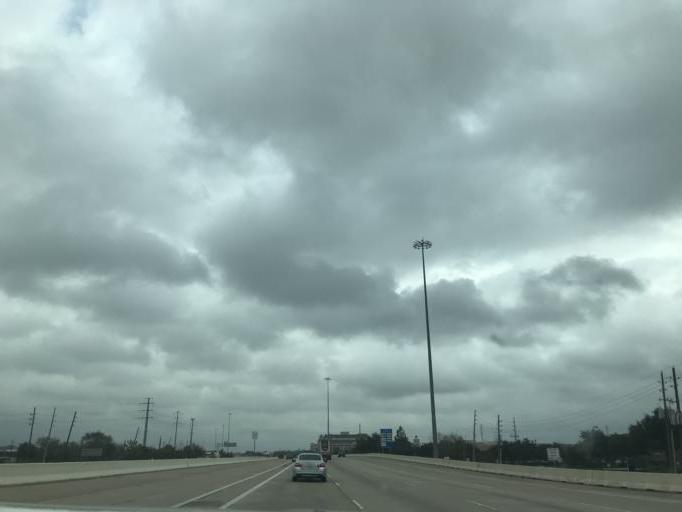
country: US
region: Texas
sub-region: Fort Bend County
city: Sugar Land
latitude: 29.5918
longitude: -95.6308
